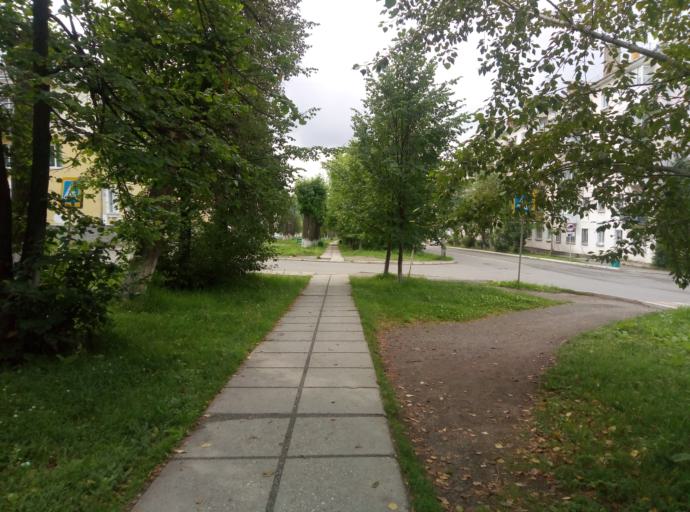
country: RU
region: Sverdlovsk
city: Krasnotur'insk
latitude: 59.7622
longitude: 60.2010
